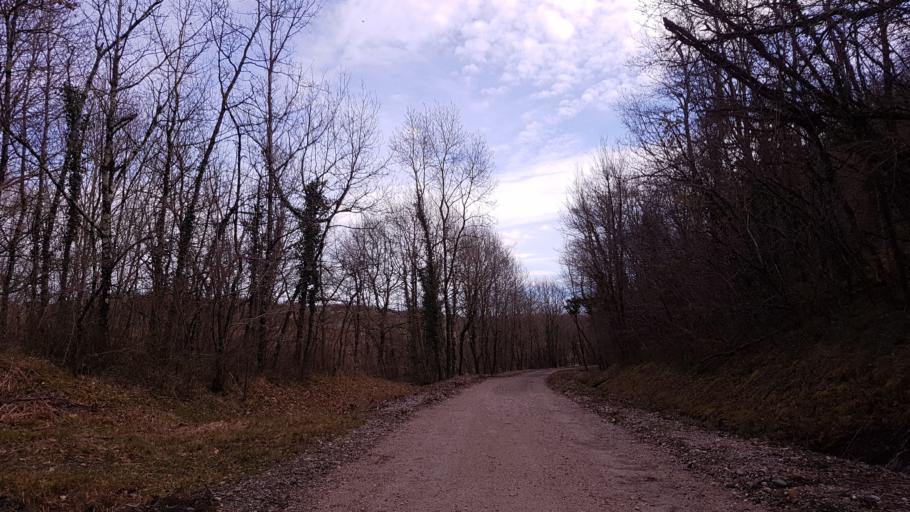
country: FR
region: Languedoc-Roussillon
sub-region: Departement de l'Aude
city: Chalabre
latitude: 43.0087
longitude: 1.9843
